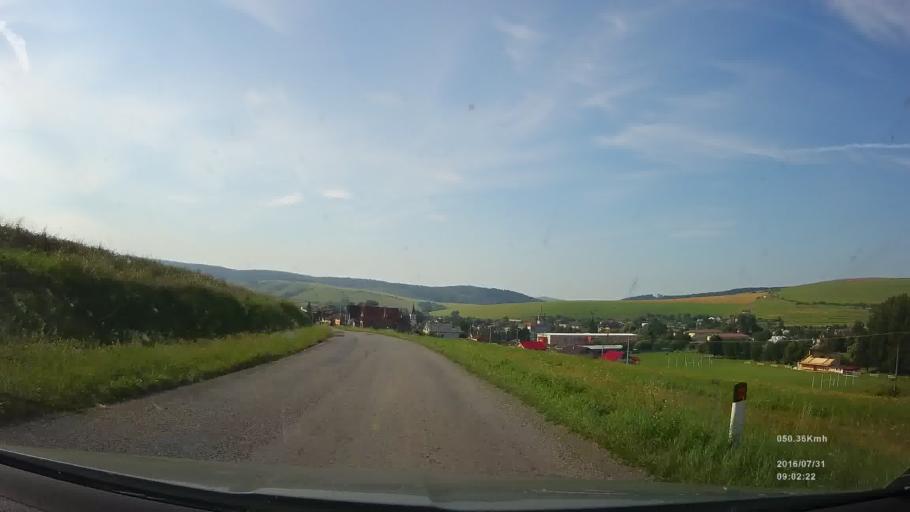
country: SK
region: Presovsky
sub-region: Okres Bardejov
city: Bardejov
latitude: 49.1553
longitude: 21.3229
